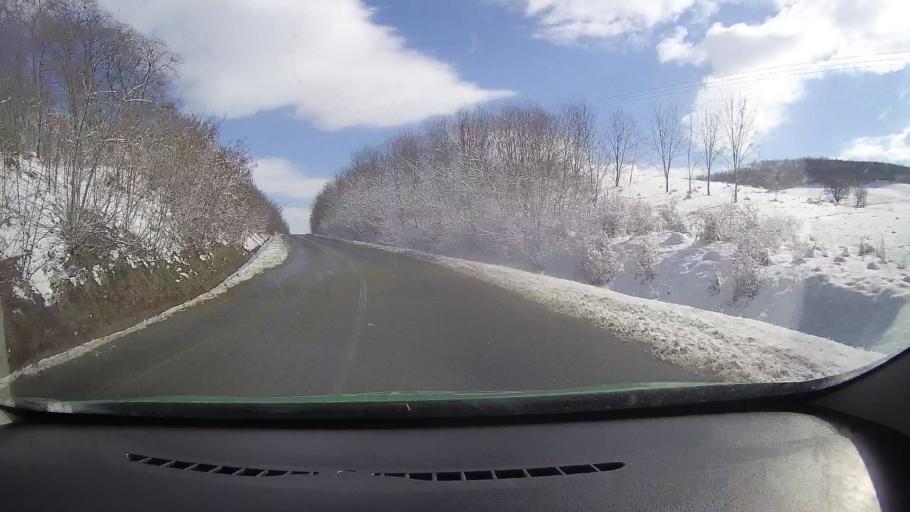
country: RO
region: Sibiu
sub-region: Comuna Barghis
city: Barghis
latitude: 45.9807
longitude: 24.5108
